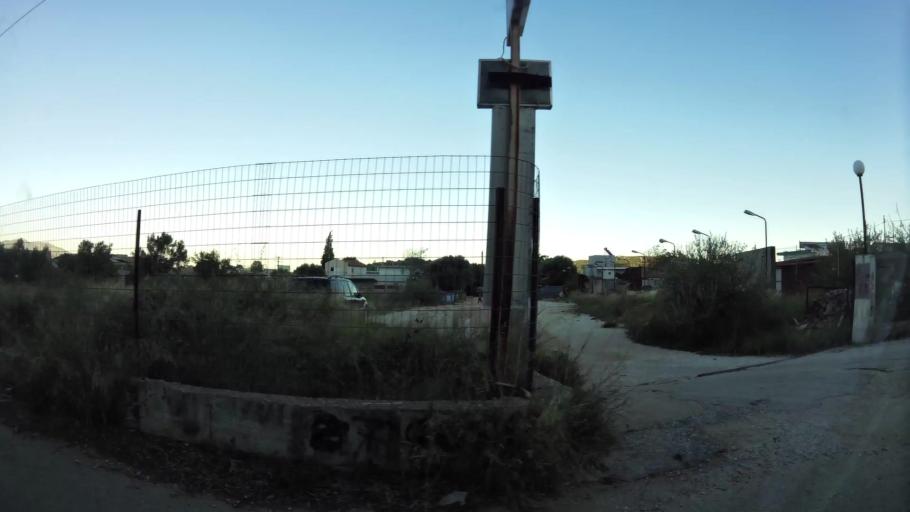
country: GR
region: Attica
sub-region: Nomarchia Anatolikis Attikis
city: Paiania
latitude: 37.9708
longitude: 23.8517
